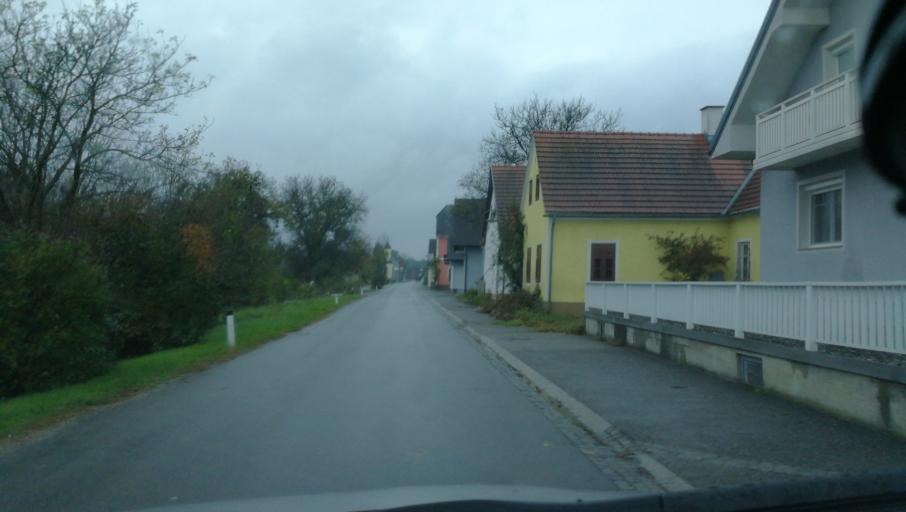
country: AT
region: Styria
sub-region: Politischer Bezirk Leibnitz
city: Spielfeld
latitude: 46.7347
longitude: 15.6659
